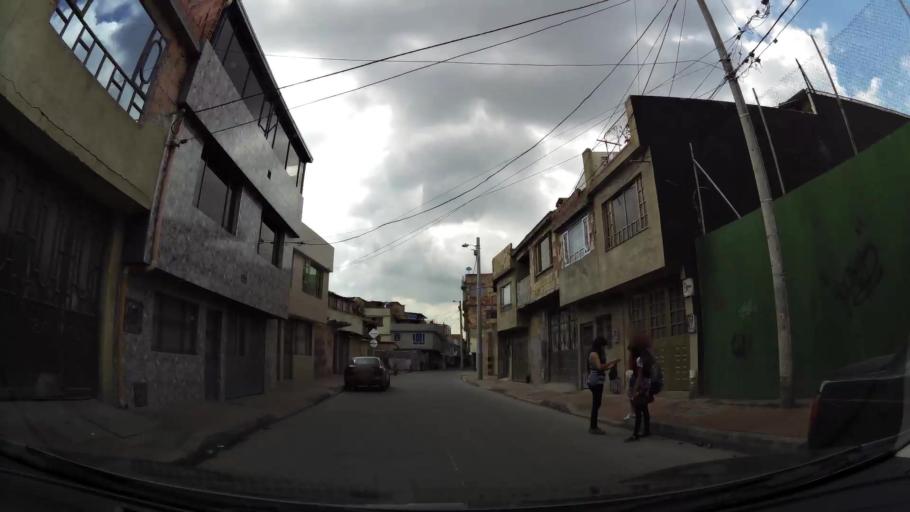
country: CO
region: Cundinamarca
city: Cota
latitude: 4.7223
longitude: -74.0909
